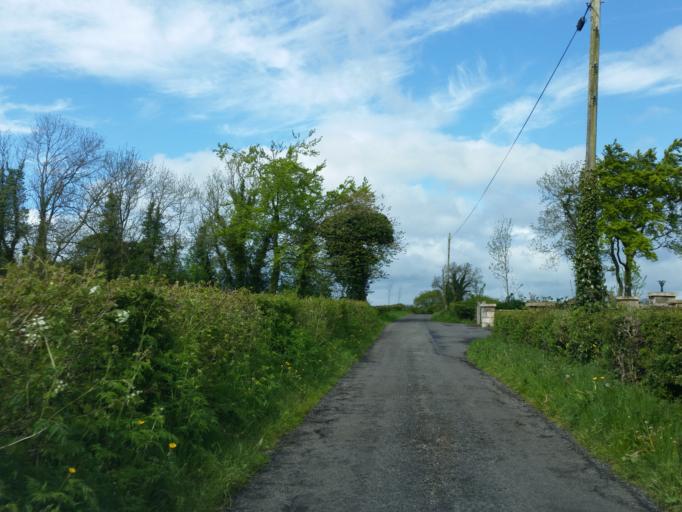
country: GB
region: Northern Ireland
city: Lisnaskea
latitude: 54.2561
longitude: -7.4067
